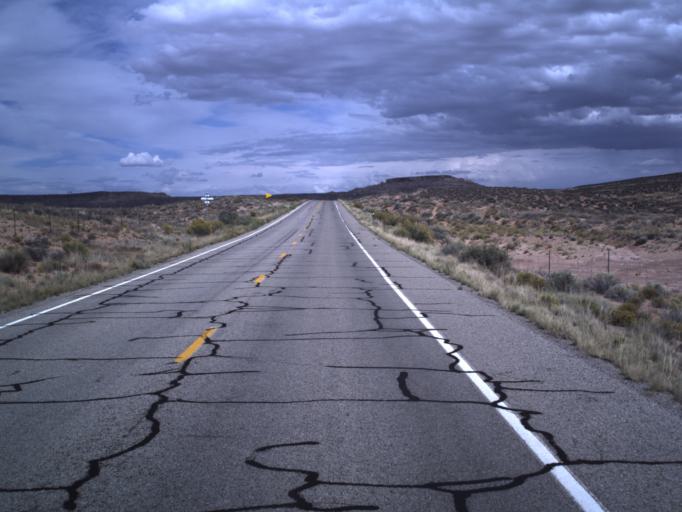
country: US
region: Utah
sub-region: San Juan County
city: Blanding
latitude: 37.2943
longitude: -109.4851
